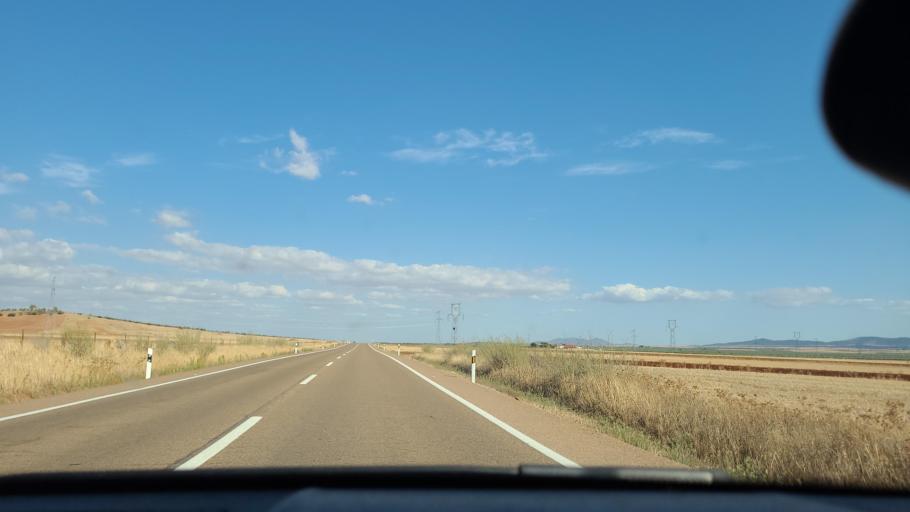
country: ES
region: Extremadura
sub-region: Provincia de Badajoz
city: Usagre
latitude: 38.3594
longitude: -6.2162
